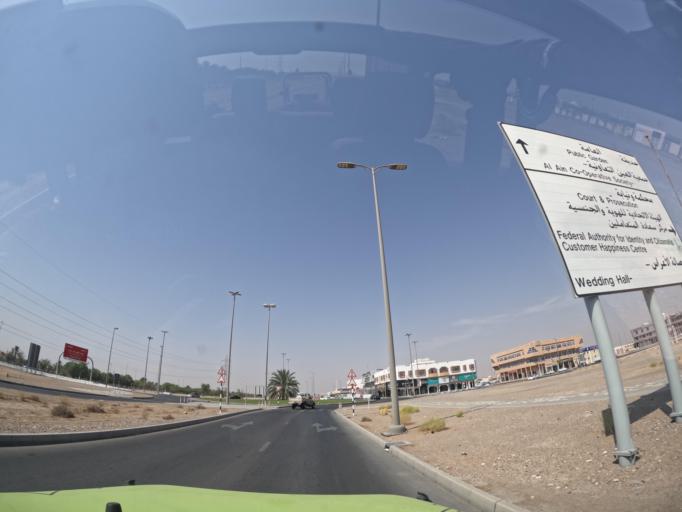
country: AE
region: Abu Dhabi
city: Al Ain
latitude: 24.2244
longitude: 55.5541
